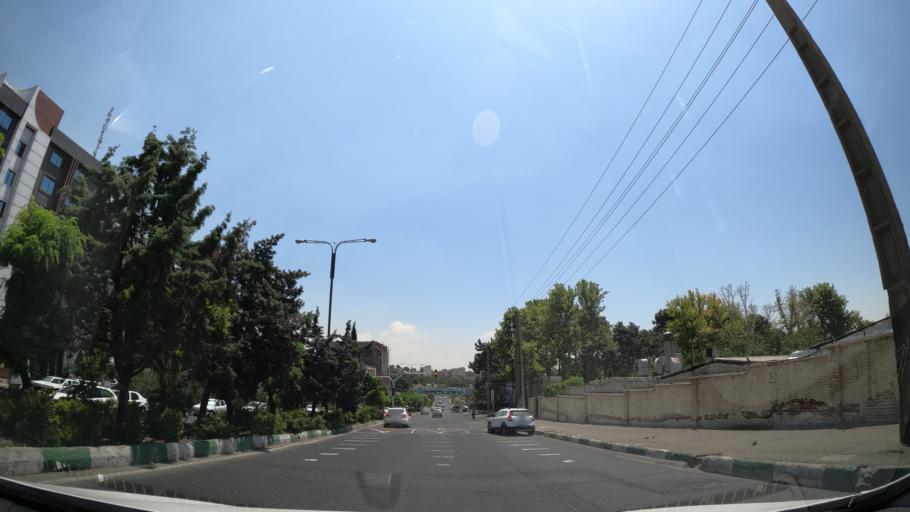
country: IR
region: Tehran
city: Tajrish
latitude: 35.7708
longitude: 51.3829
